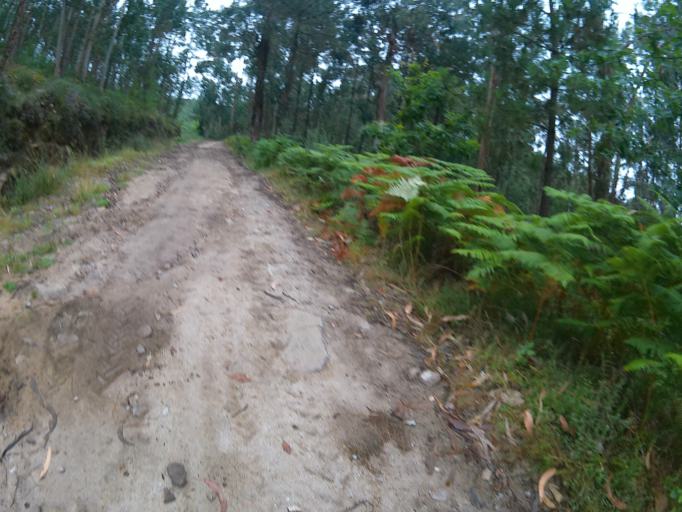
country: PT
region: Viana do Castelo
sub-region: Ponte de Lima
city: Ponte de Lima
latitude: 41.7337
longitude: -8.6033
